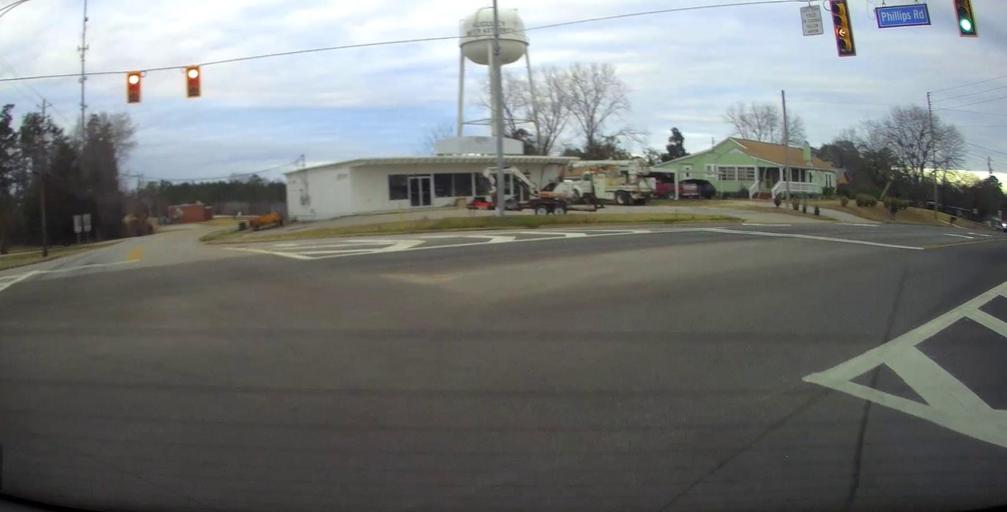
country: US
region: Alabama
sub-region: Chambers County
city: Huguley
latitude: 32.8463
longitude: -85.2327
